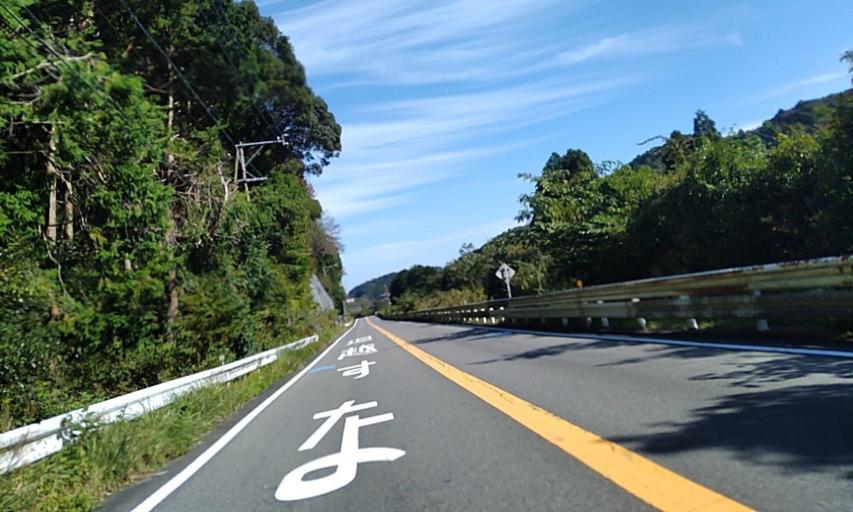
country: JP
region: Mie
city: Owase
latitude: 34.1587
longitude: 136.2682
